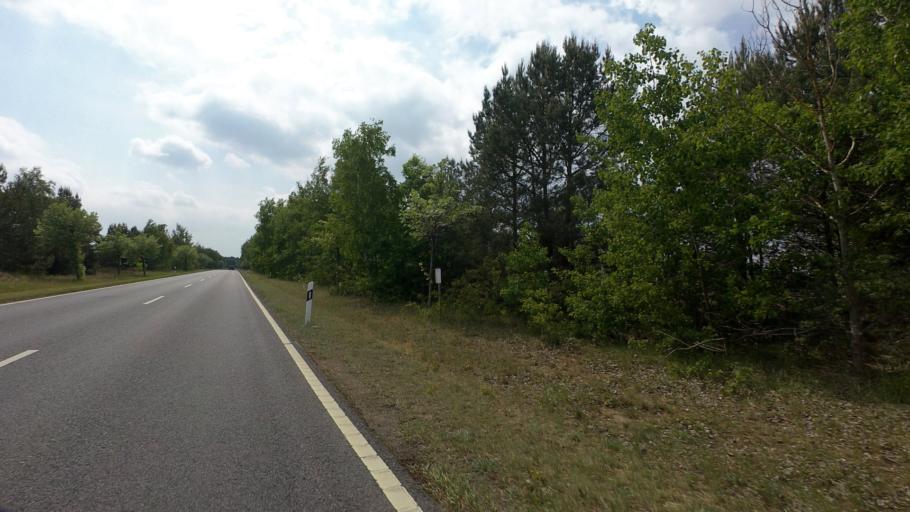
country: DE
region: Brandenburg
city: Drachhausen
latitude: 51.9386
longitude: 14.3410
